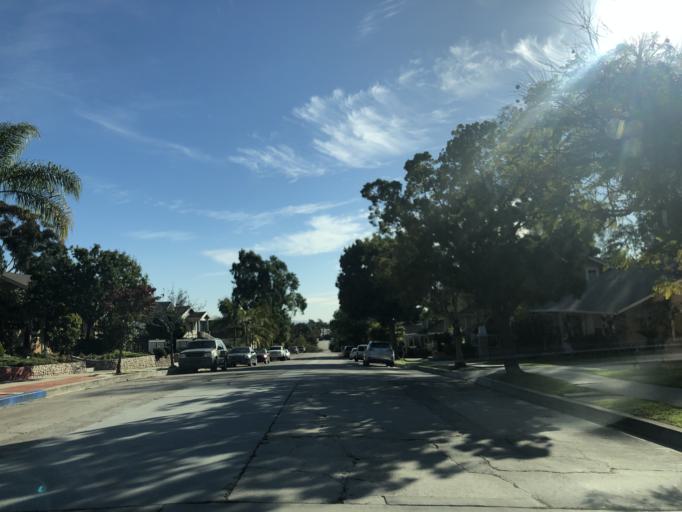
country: US
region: California
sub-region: San Diego County
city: San Diego
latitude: 32.7262
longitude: -117.1266
